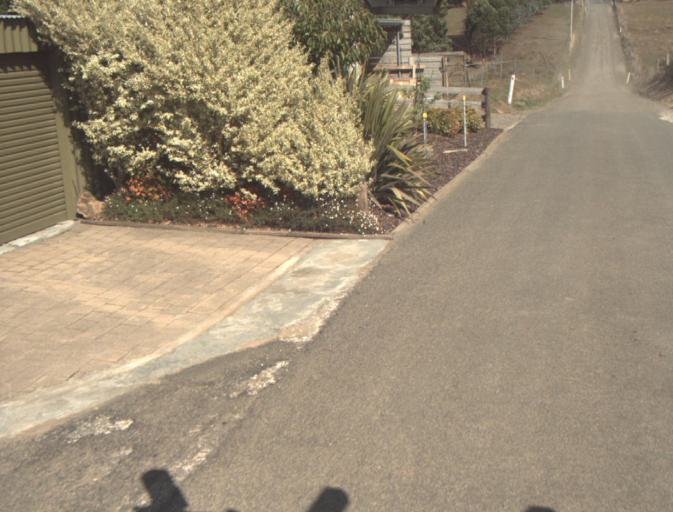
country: AU
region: Tasmania
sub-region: Launceston
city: Mayfield
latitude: -41.2271
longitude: 147.2364
